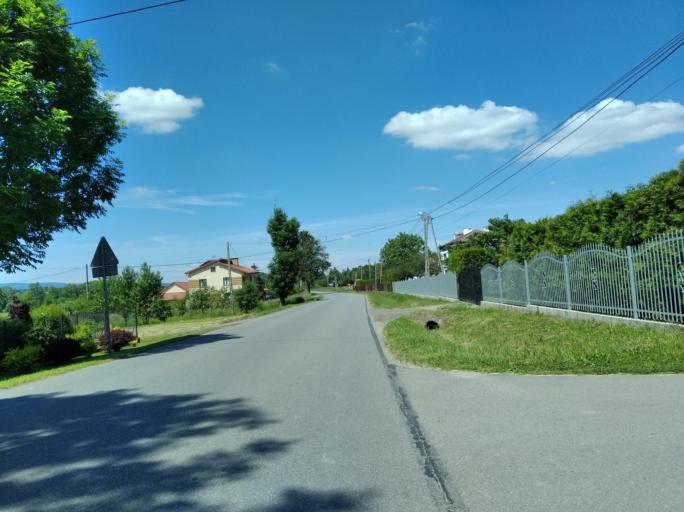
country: PL
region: Subcarpathian Voivodeship
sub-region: Powiat jasielski
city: Nowy Zmigrod
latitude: 49.6192
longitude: 21.5558
